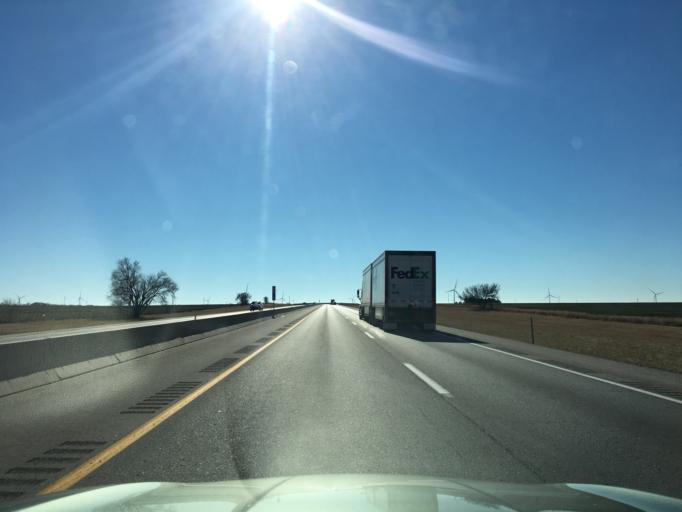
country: US
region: Kansas
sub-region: Sumner County
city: Wellington
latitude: 37.1675
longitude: -97.3396
